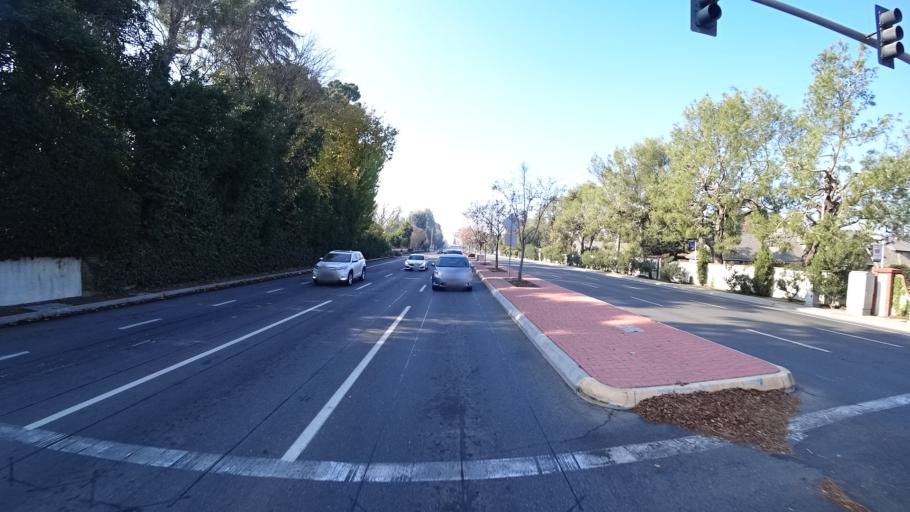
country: US
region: California
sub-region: Kern County
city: Greenacres
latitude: 35.3543
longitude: -119.0758
